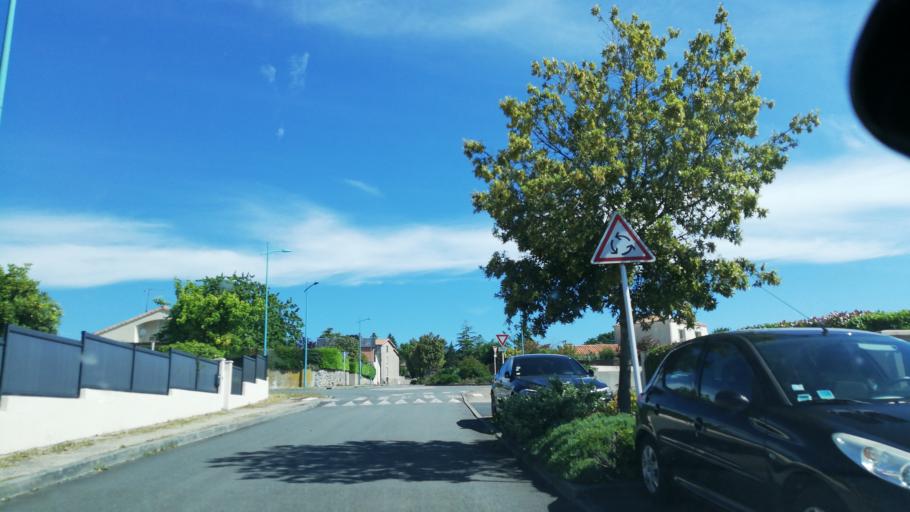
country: FR
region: Poitou-Charentes
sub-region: Departement des Deux-Sevres
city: Moncoutant
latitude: 46.7162
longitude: -0.5876
